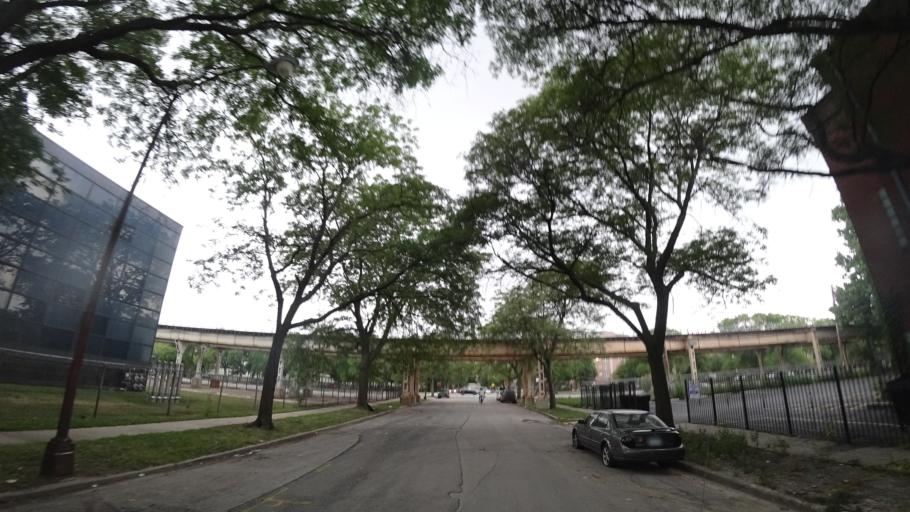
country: US
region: Illinois
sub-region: Cook County
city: Chicago
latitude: 41.8396
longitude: -87.6255
